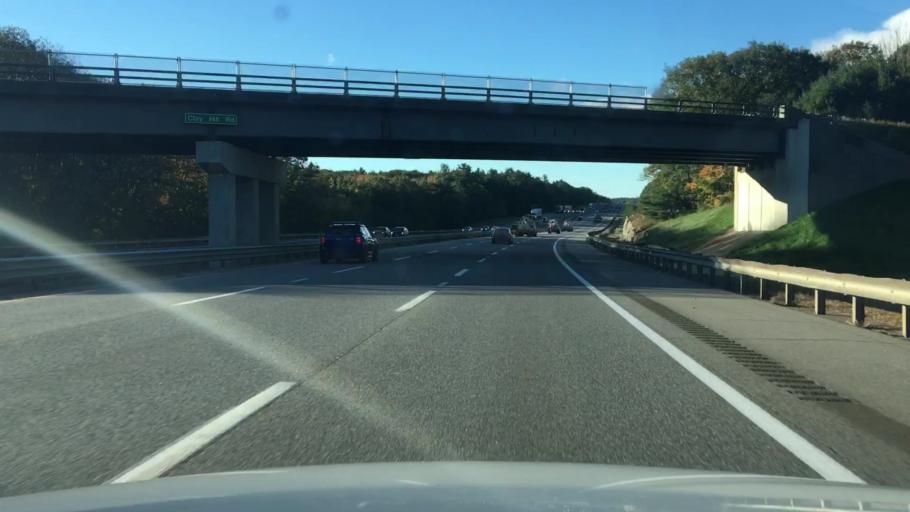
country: US
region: Maine
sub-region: York County
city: Cape Neddick
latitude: 43.2239
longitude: -70.6373
